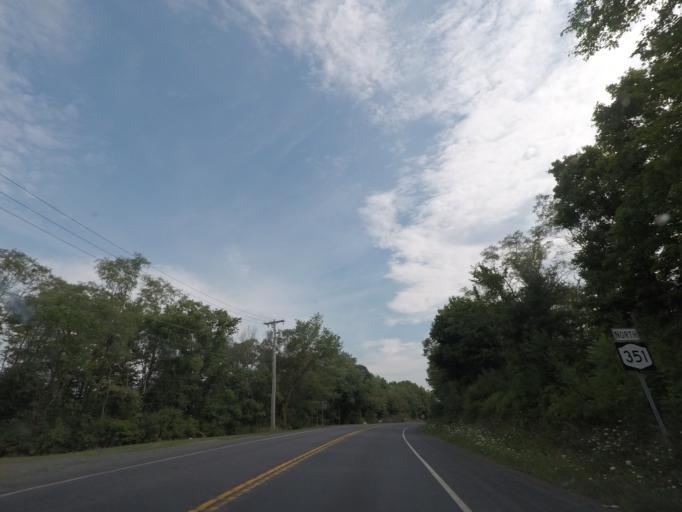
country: US
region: New York
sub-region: Rensselaer County
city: Poestenkill
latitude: 42.6645
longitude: -73.5796
